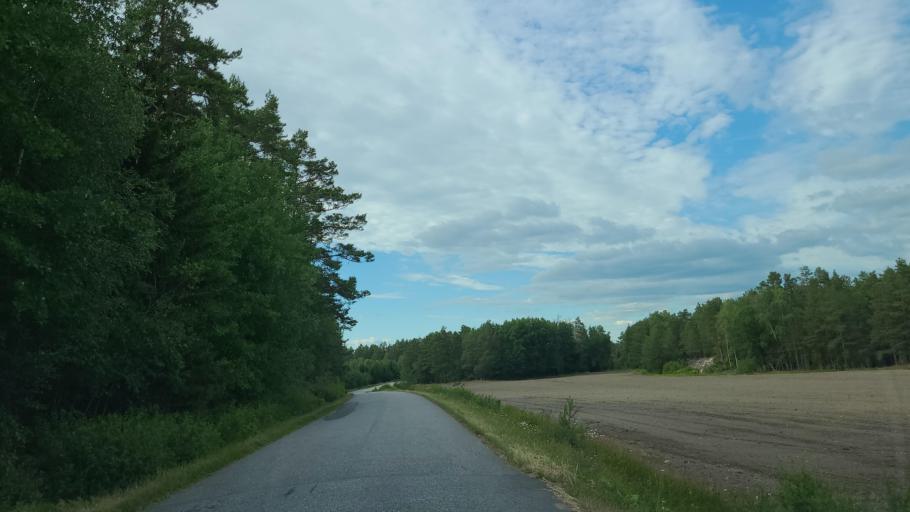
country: FI
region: Varsinais-Suomi
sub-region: Turku
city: Rymaettylae
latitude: 60.3048
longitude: 21.9413
